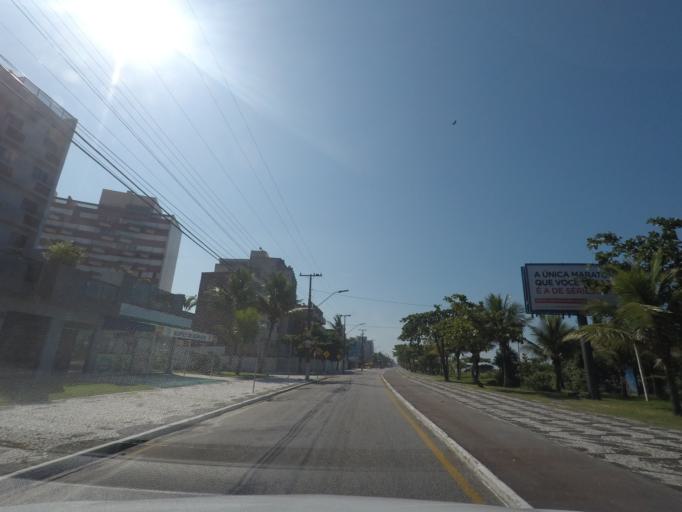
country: BR
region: Parana
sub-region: Guaratuba
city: Guaratuba
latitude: -25.8320
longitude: -48.5367
